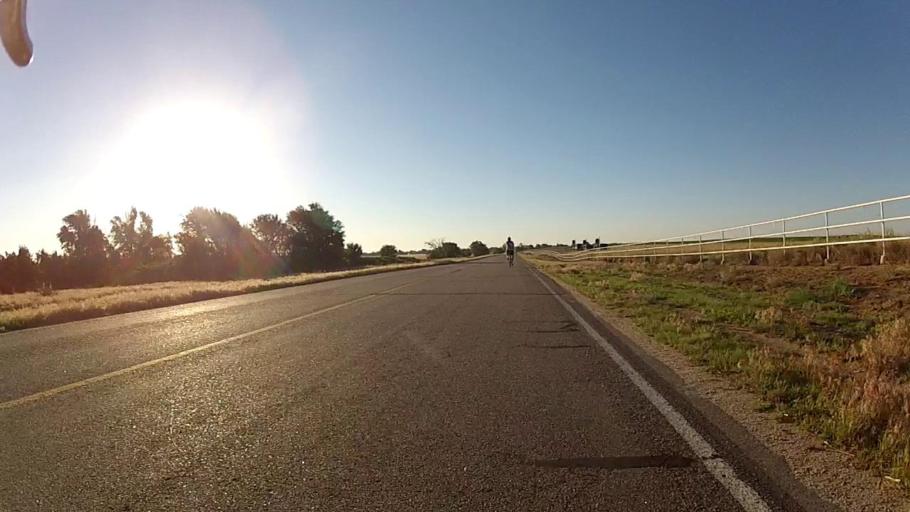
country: US
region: Kansas
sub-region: Ford County
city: Dodge City
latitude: 37.7195
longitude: -99.9471
